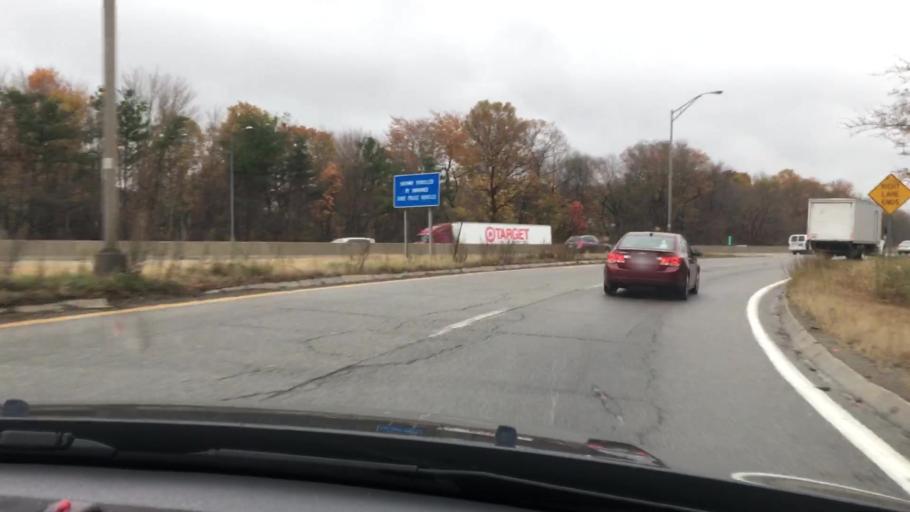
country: US
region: Massachusetts
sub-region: Worcester County
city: Westborough
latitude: 42.2635
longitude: -71.5728
